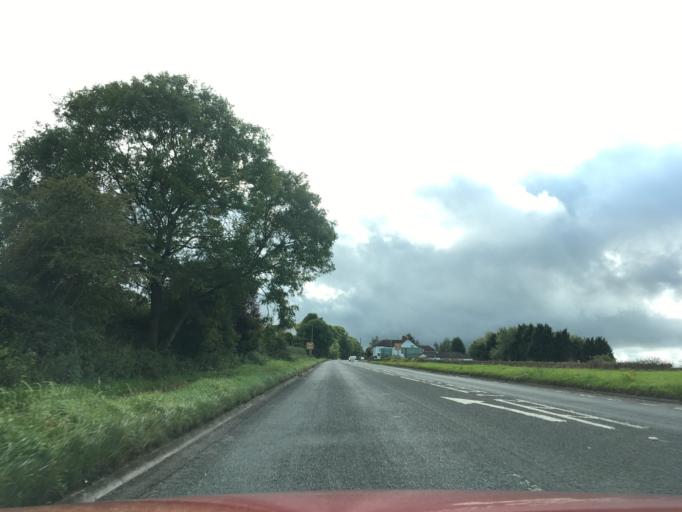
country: GB
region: England
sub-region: South Gloucestershire
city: Tytherington
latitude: 51.6123
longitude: -2.4850
